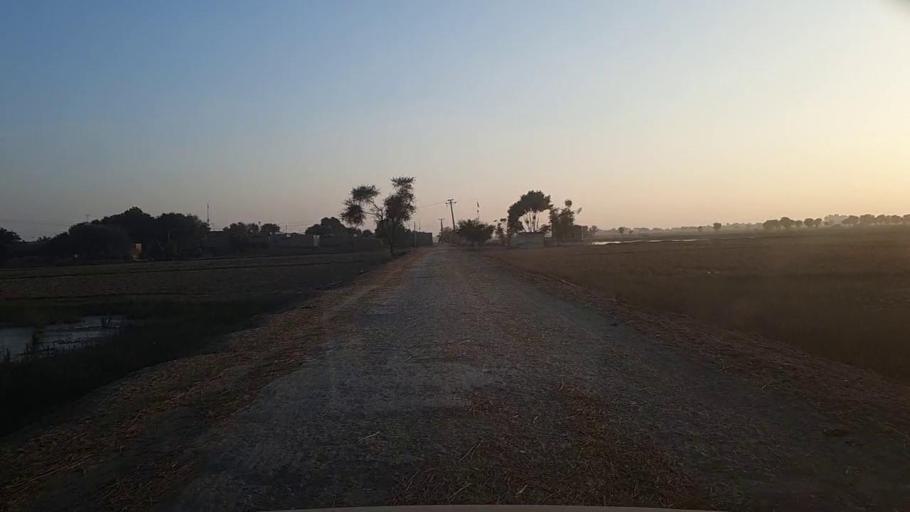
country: PK
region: Sindh
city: Khairpur Nathan Shah
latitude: 27.1718
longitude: 67.7331
